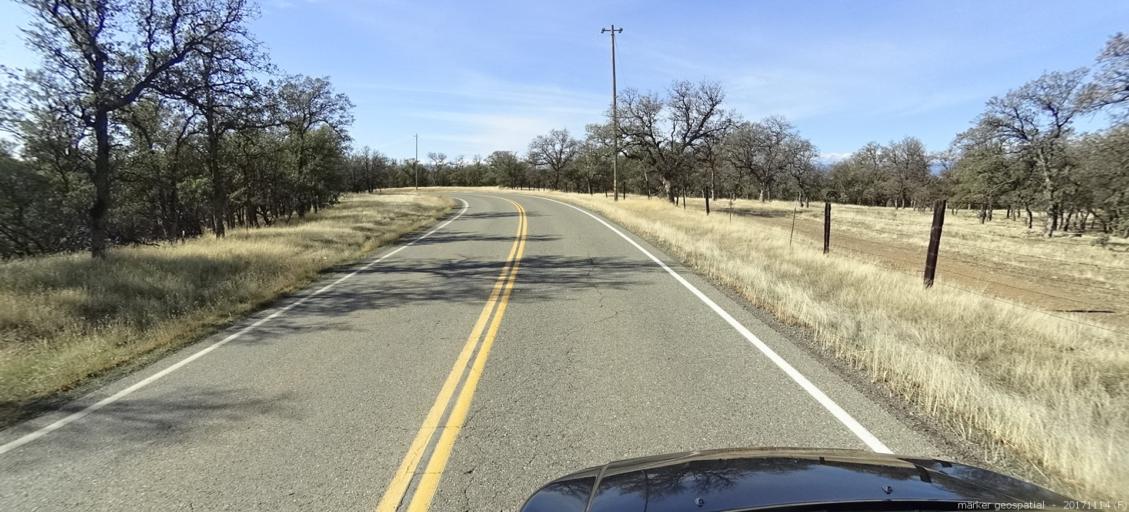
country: US
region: California
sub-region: Shasta County
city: Anderson
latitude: 40.4229
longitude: -122.3348
